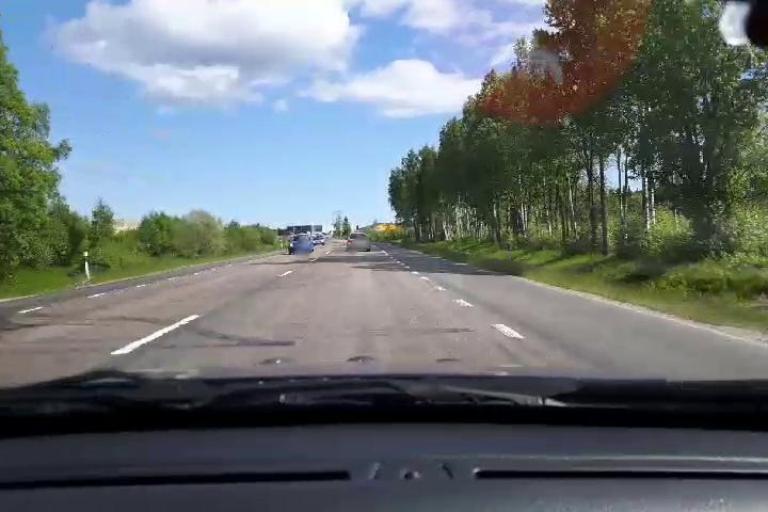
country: SE
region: Gaevleborg
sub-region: Hudiksvalls Kommun
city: Sorforsa
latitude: 61.7159
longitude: 17.0355
